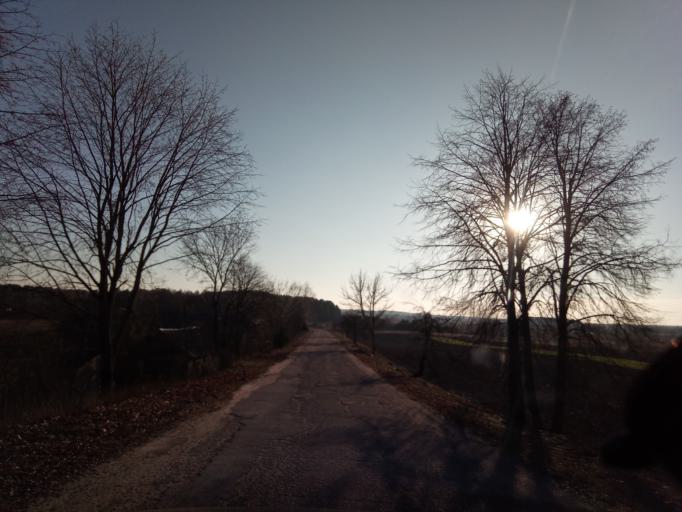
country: LT
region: Alytaus apskritis
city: Druskininkai
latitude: 53.9784
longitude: 23.9456
